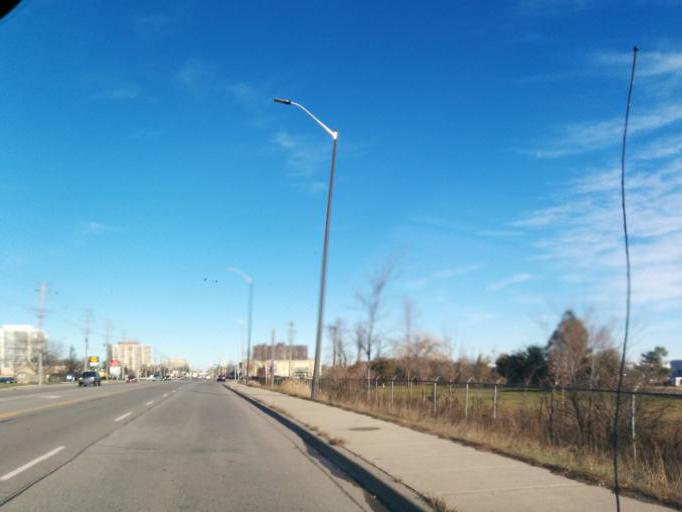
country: CA
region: Ontario
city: Oakville
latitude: 43.5066
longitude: -79.6347
